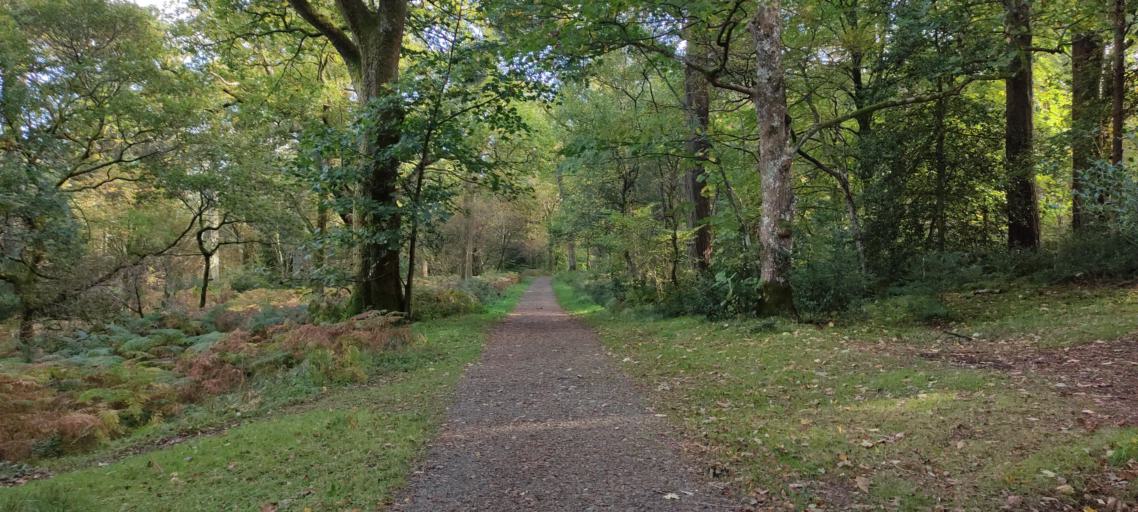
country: GB
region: England
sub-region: Cumbria
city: Cockermouth
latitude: 54.5840
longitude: -3.3638
